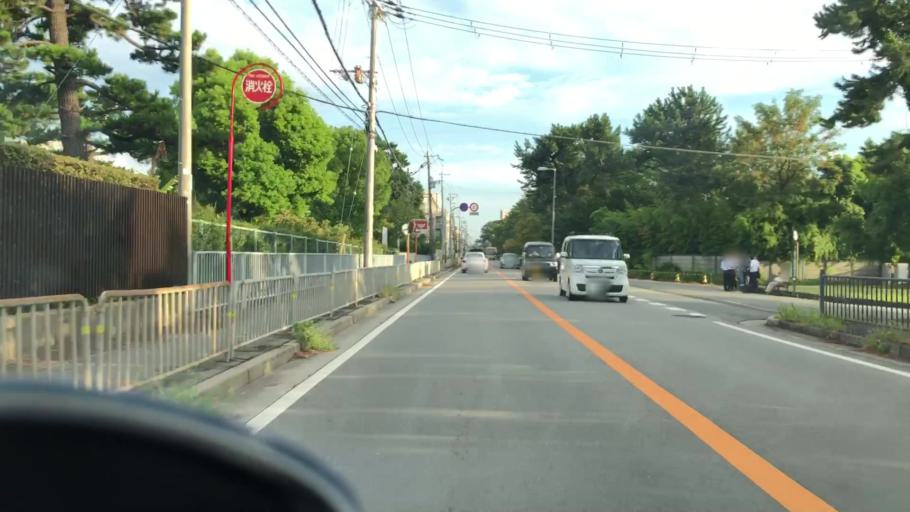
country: JP
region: Hyogo
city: Takarazuka
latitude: 34.7799
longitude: 135.3709
